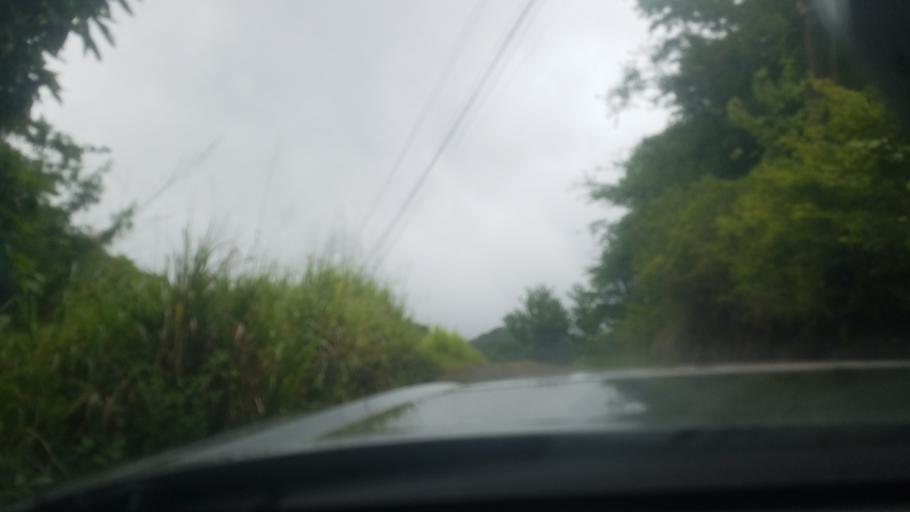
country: LC
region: Gros-Islet
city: Gros Islet
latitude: 14.0495
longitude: -60.9359
